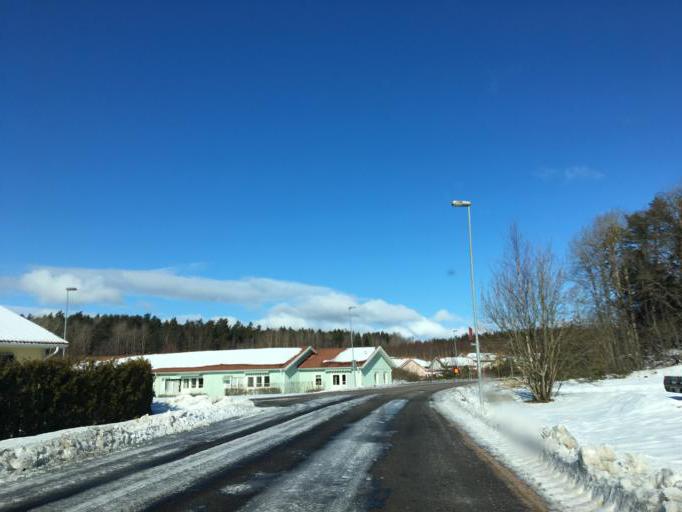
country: SE
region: Vaestmanland
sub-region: Vasteras
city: Vasteras
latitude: 59.6231
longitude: 16.4796
